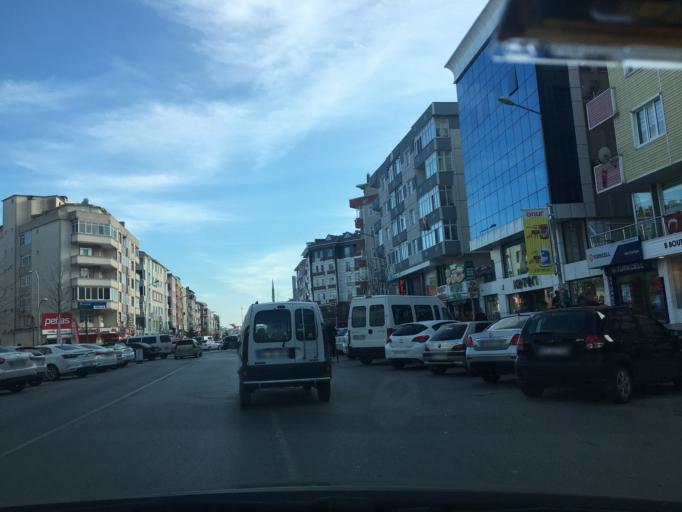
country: TR
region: Tekirdag
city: Cerkezkoey
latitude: 41.2908
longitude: 27.9985
